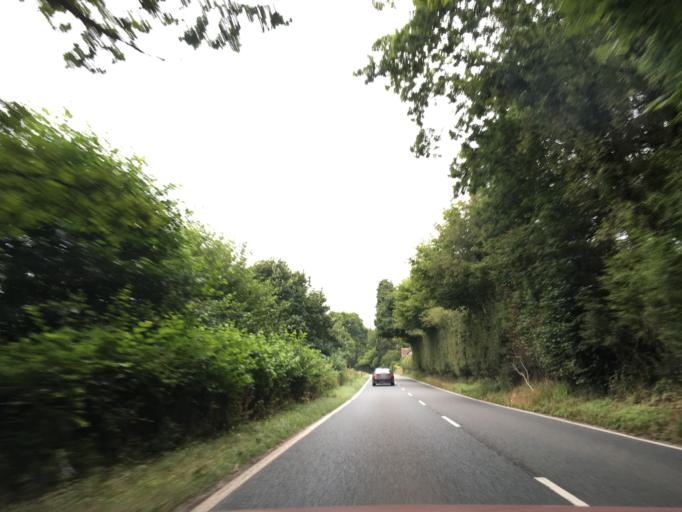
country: GB
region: Wales
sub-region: Blaenau Gwent
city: Brynmawr
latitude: 51.8683
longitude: -3.1544
